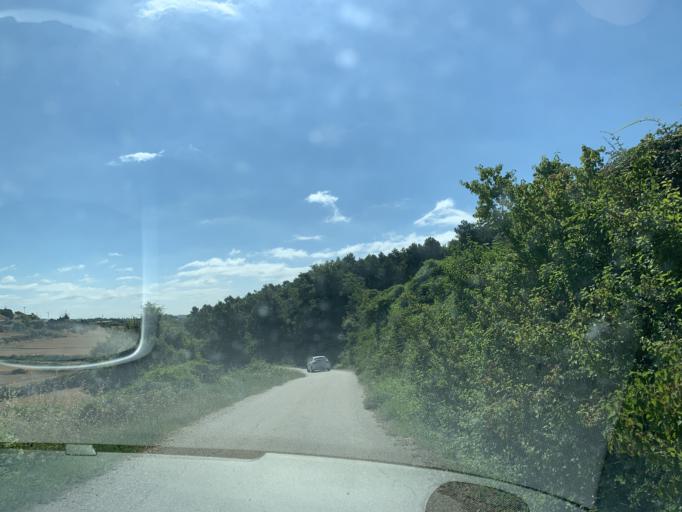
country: ES
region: Catalonia
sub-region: Provincia de Tarragona
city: Conesa
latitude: 41.5413
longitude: 1.2921
